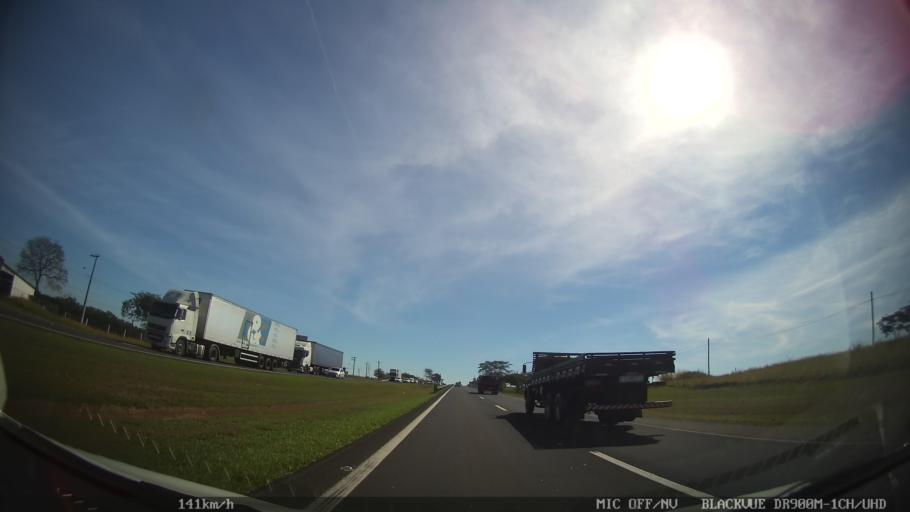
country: BR
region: Sao Paulo
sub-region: Pirassununga
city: Pirassununga
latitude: -21.9851
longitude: -47.4502
